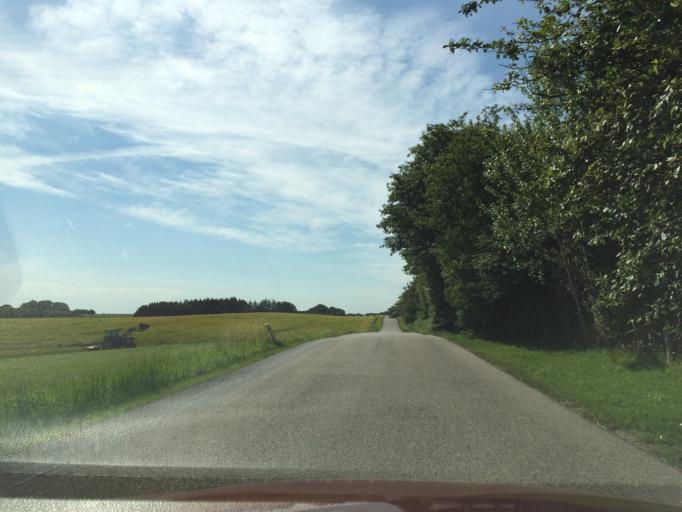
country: DK
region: Central Jutland
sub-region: Silkeborg Kommune
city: Svejbaek
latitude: 56.2252
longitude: 9.6217
